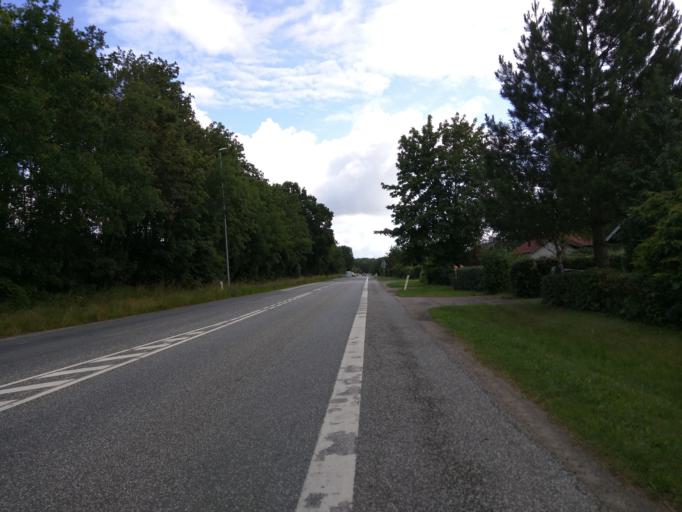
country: DK
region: Zealand
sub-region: Kalundborg Kommune
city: Svebolle
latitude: 55.6766
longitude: 11.2963
